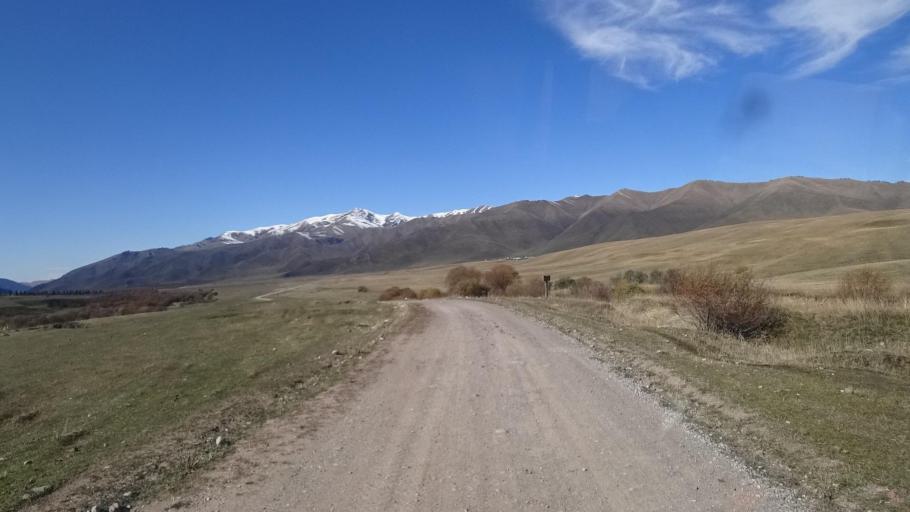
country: KZ
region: Almaty Oblysy
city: Kegen
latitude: 42.7356
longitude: 79.0172
